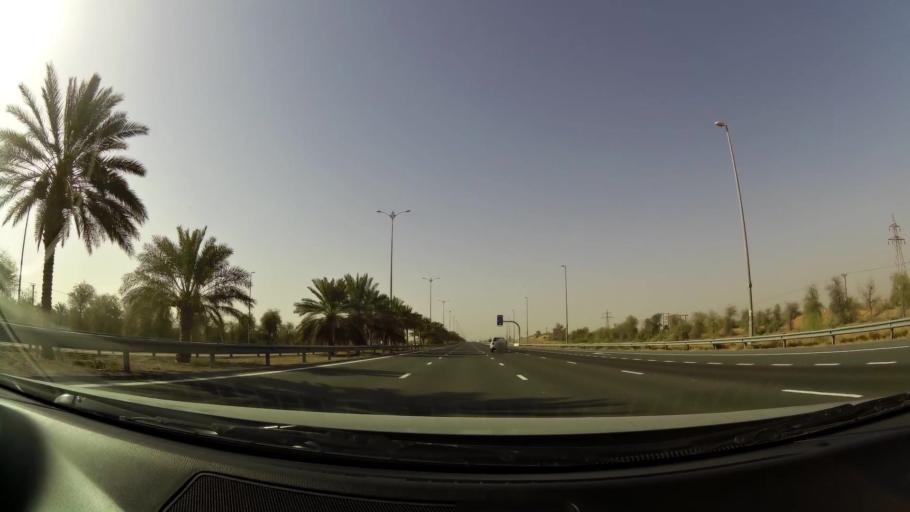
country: OM
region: Al Buraimi
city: Al Buraymi
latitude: 24.5249
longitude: 55.7612
